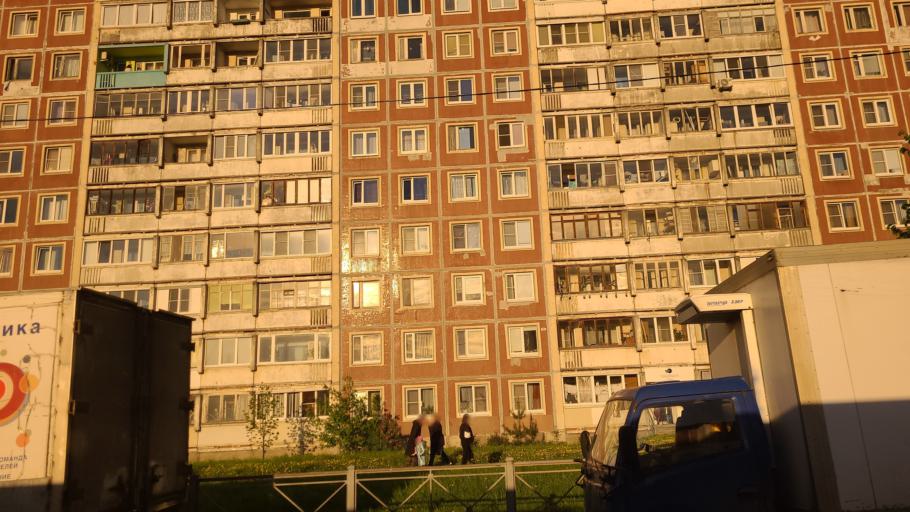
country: RU
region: St.-Petersburg
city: Kolpino
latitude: 59.7374
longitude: 30.5799
